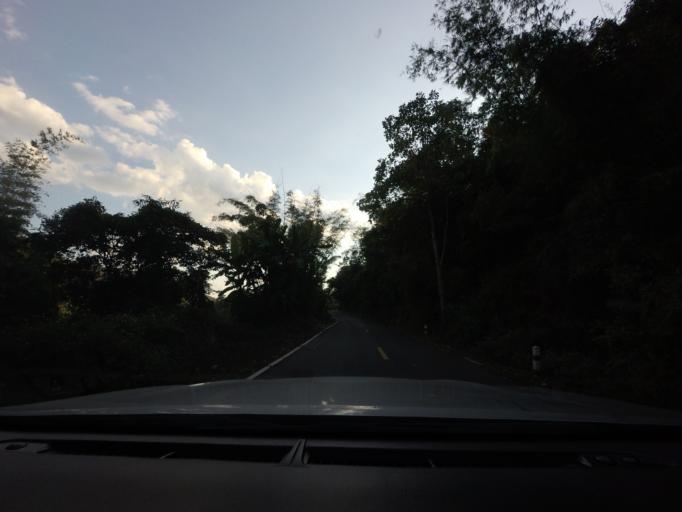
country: TH
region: Chiang Mai
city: Chai Prakan
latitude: 19.5579
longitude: 99.1671
